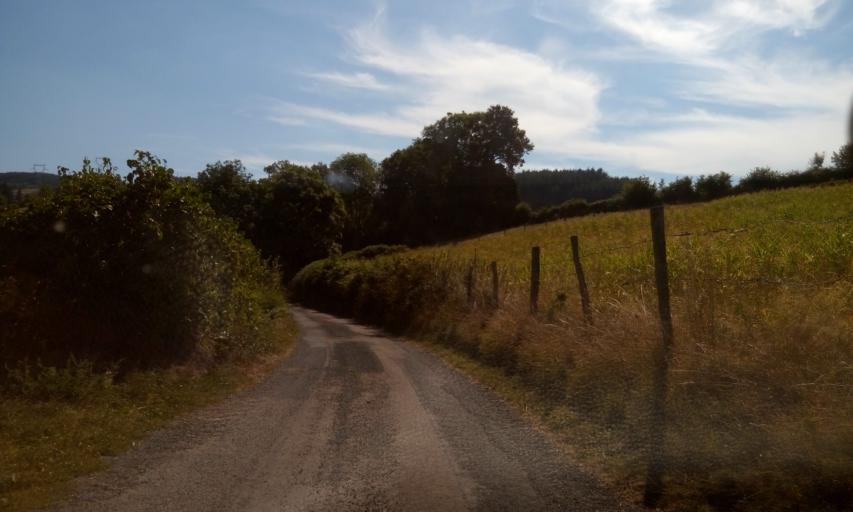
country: FR
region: Rhone-Alpes
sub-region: Departement du Rhone
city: Amplepuis
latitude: 45.9649
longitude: 4.3581
